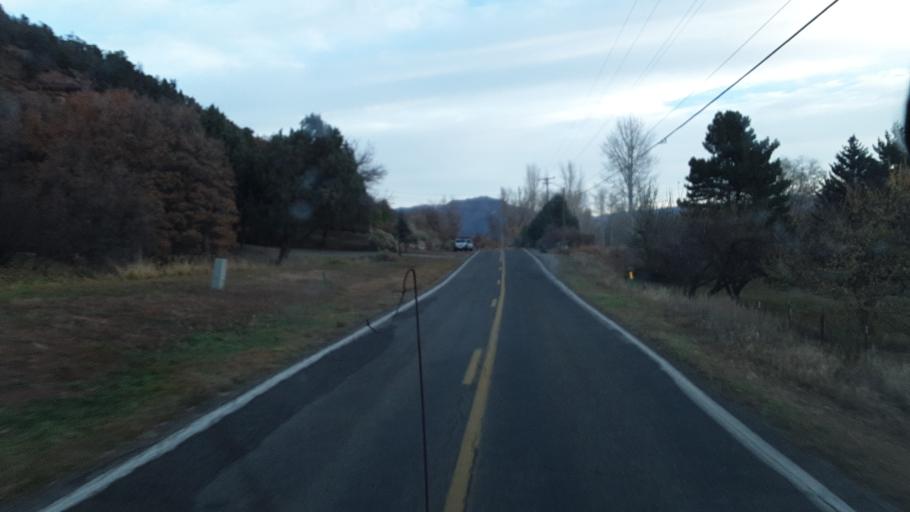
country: US
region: Colorado
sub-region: La Plata County
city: Durango
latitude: 37.3549
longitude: -107.8558
